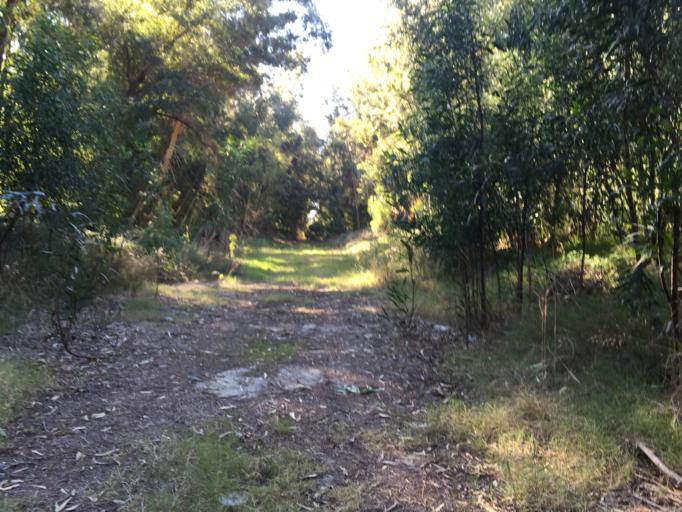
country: CY
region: Larnaka
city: Kolossi
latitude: 34.6269
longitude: 32.9478
